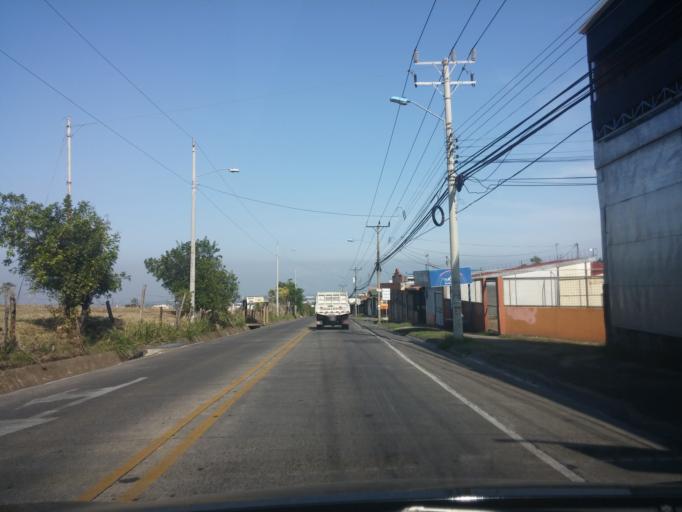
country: CR
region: Heredia
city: Llorente
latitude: 9.9921
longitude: -84.1443
